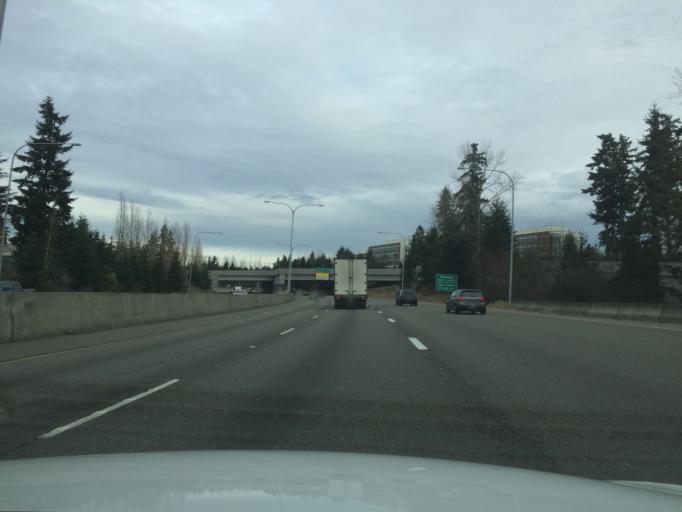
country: US
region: Washington
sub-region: King County
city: Redmond
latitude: 47.6374
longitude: -122.1377
